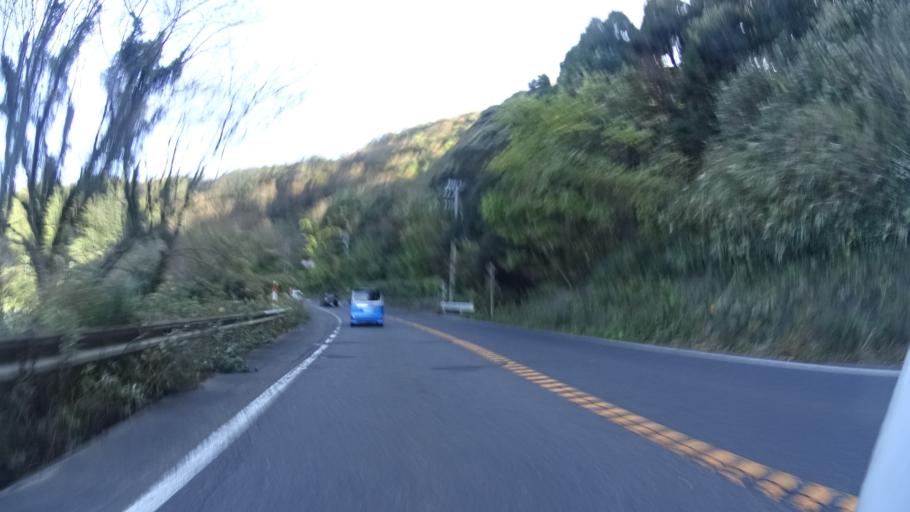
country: JP
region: Fukui
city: Tsuruga
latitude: 35.6977
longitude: 136.0812
